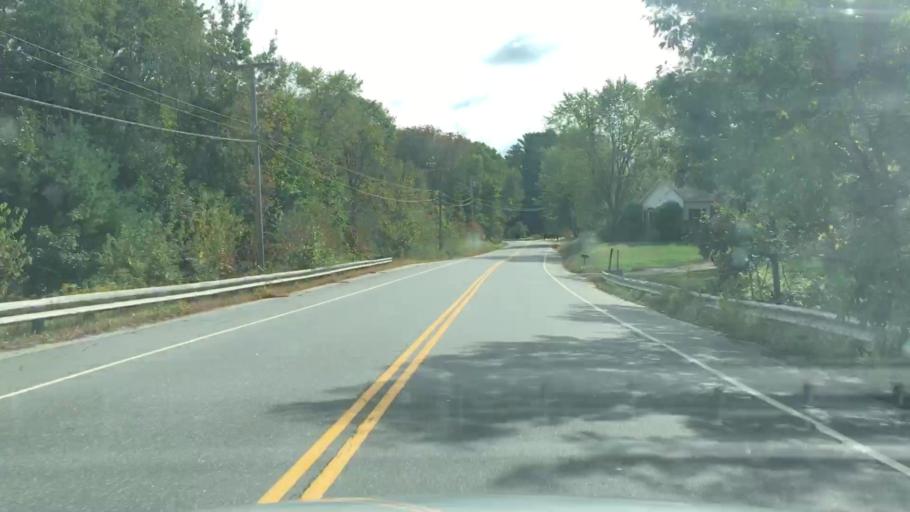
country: US
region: Maine
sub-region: Androscoggin County
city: Lewiston
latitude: 44.0373
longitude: -70.1891
